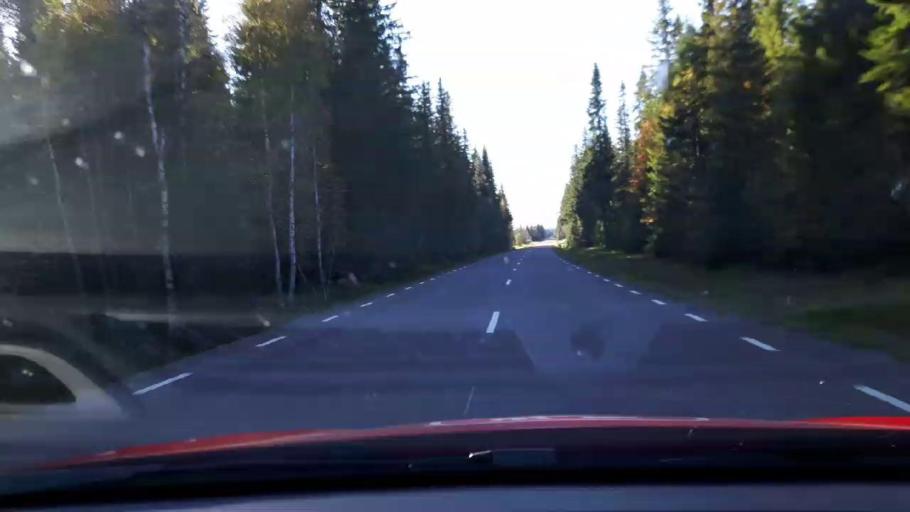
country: SE
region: Jaemtland
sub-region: Stroemsunds Kommun
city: Stroemsund
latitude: 63.8453
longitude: 15.3010
